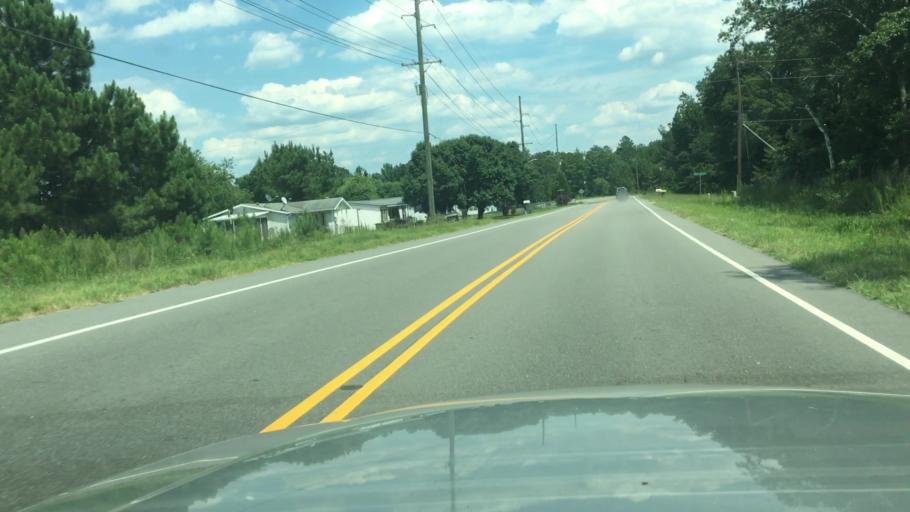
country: US
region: North Carolina
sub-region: Cumberland County
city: Hope Mills
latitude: 34.9475
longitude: -78.8765
